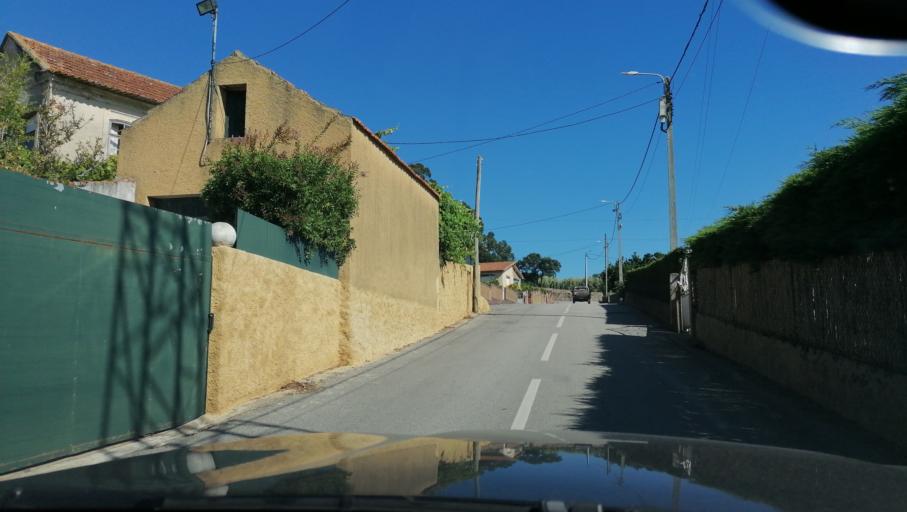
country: PT
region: Aveiro
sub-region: Estarreja
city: Beduido
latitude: 40.7539
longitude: -8.5596
